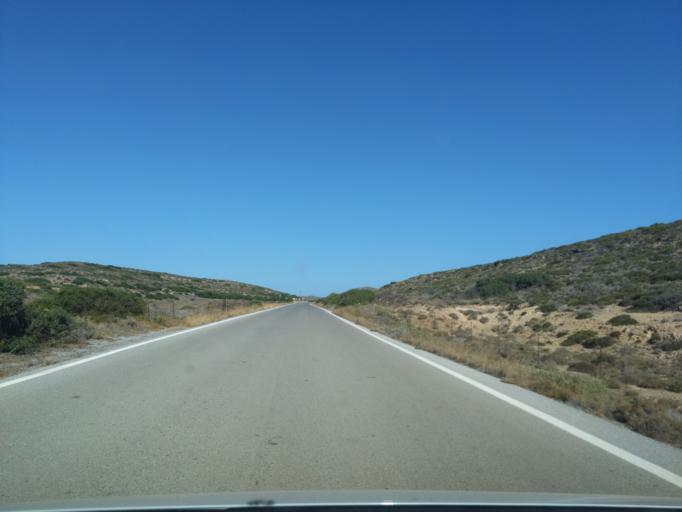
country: GR
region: Crete
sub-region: Nomos Lasithiou
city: Palekastro
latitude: 35.2361
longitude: 26.2509
